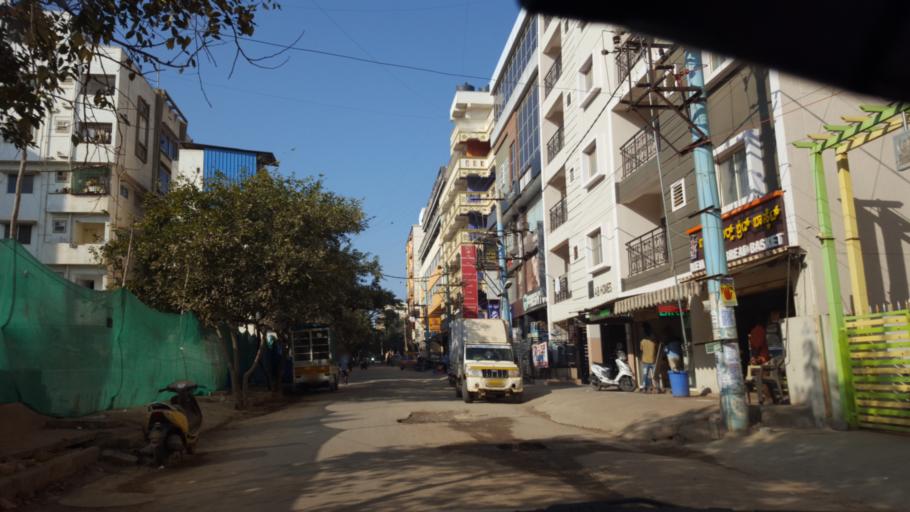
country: IN
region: Karnataka
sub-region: Bangalore Urban
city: Bangalore
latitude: 12.9502
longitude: 77.7155
